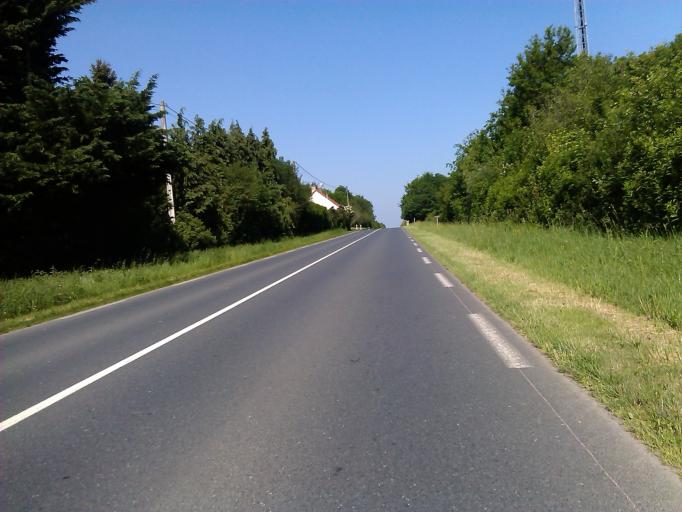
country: FR
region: Centre
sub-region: Departement de l'Indre
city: Cluis
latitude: 46.6020
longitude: 1.7223
